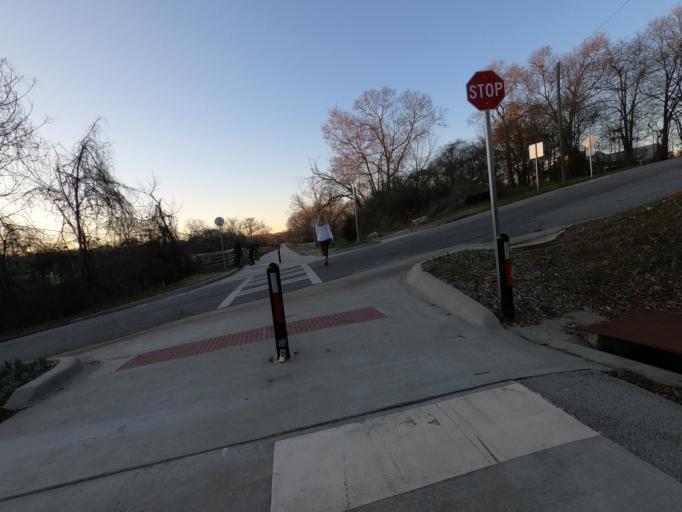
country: US
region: Georgia
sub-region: Clarke County
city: Athens
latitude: 33.9517
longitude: -83.3618
